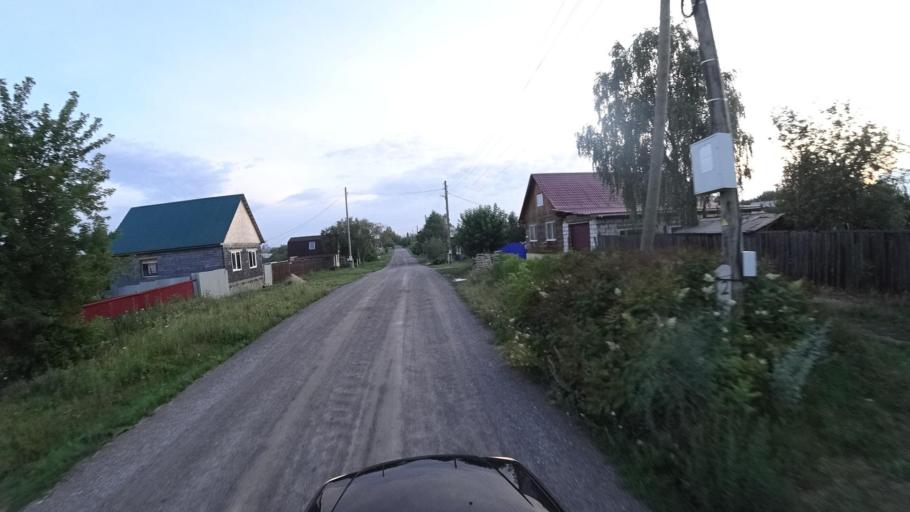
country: RU
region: Sverdlovsk
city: Kamyshlov
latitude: 56.8551
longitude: 62.7024
